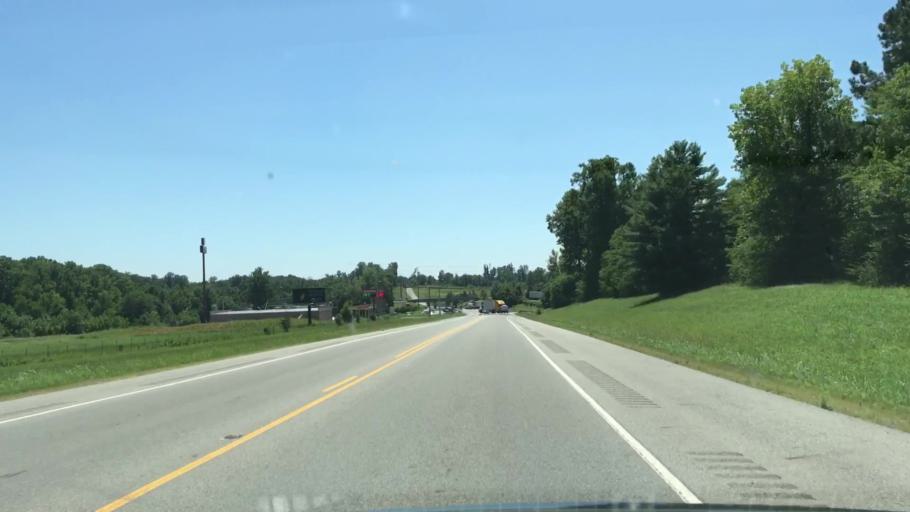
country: US
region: Tennessee
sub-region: Putnam County
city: Baxter
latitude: 36.1427
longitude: -85.6289
